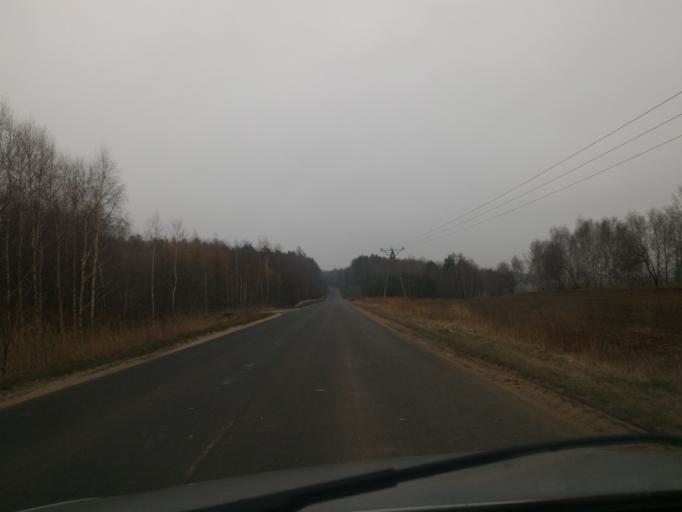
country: CZ
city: Hradek nad Nisou
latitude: 50.8834
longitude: 14.8828
